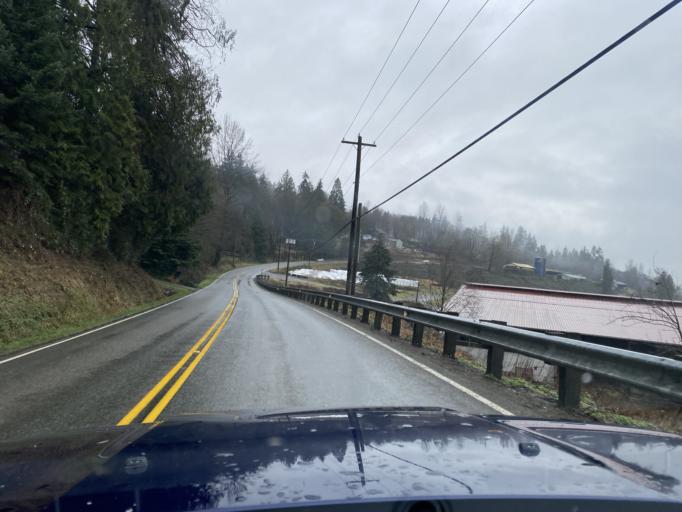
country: US
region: Washington
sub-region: King County
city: Duvall
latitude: 47.7869
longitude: -121.9994
